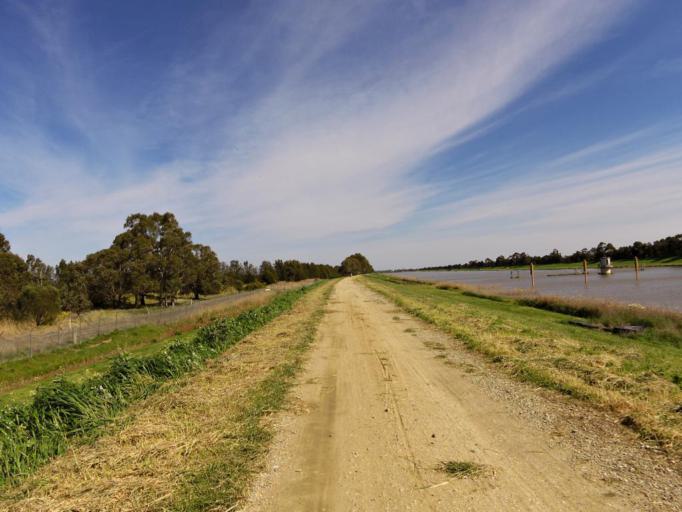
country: AU
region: Victoria
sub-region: Kingston
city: Patterson Lakes
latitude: -38.0464
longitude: 145.1725
